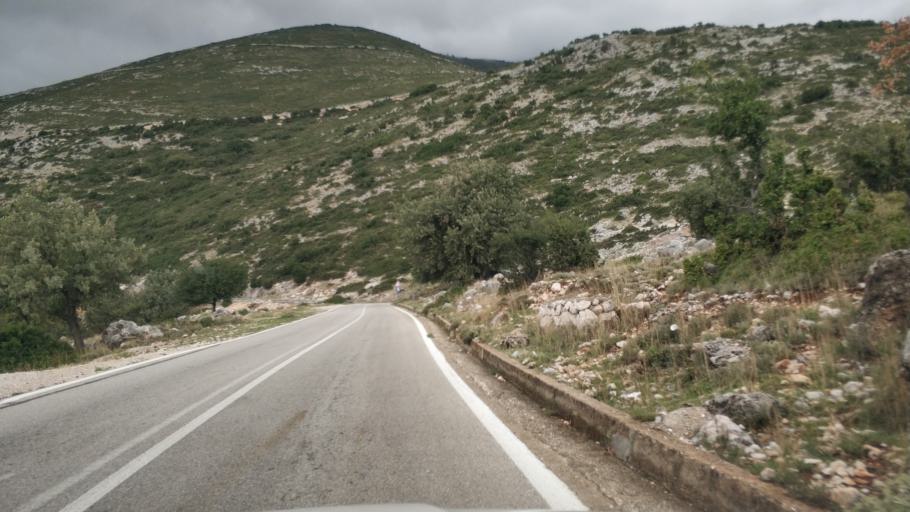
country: AL
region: Vlore
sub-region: Rrethi i Vlores
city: Vranisht
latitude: 40.1758
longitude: 19.6051
